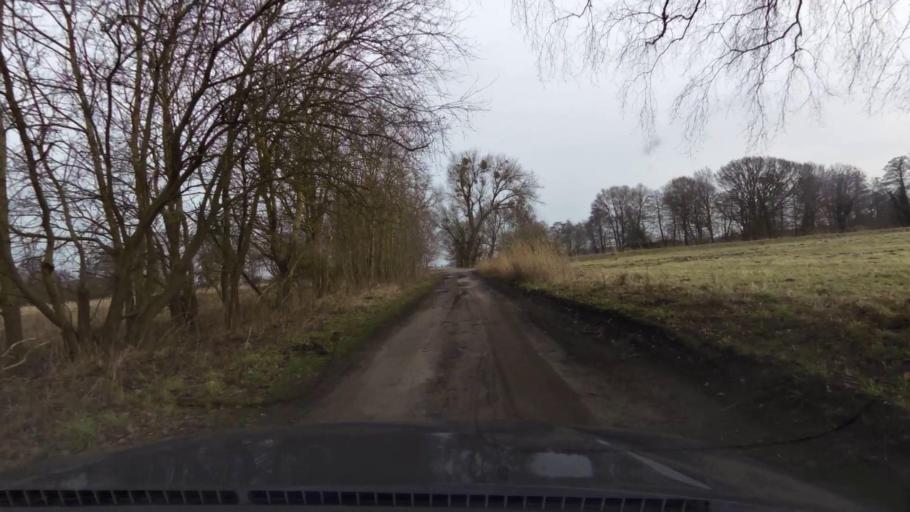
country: PL
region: West Pomeranian Voivodeship
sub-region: Powiat goleniowski
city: Stepnica
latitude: 53.7282
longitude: 14.5574
